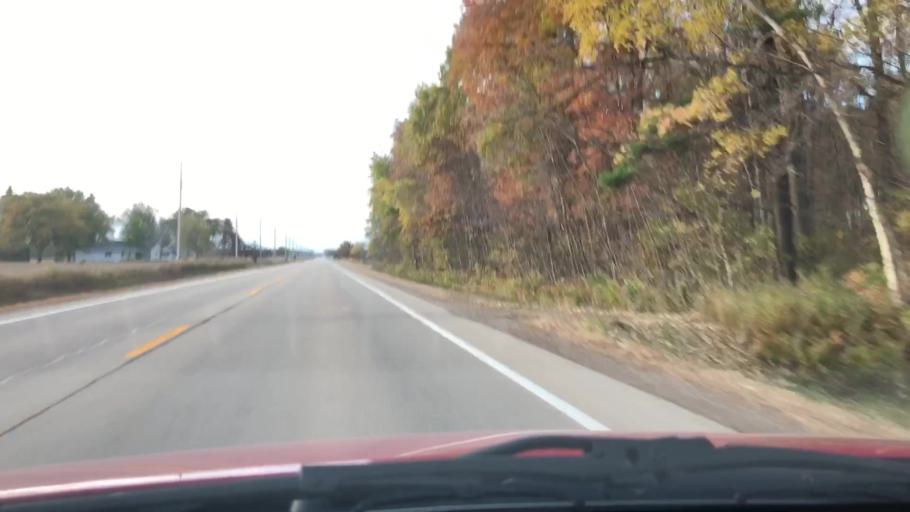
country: US
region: Wisconsin
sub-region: Outagamie County
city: Seymour
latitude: 44.4923
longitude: -88.2912
